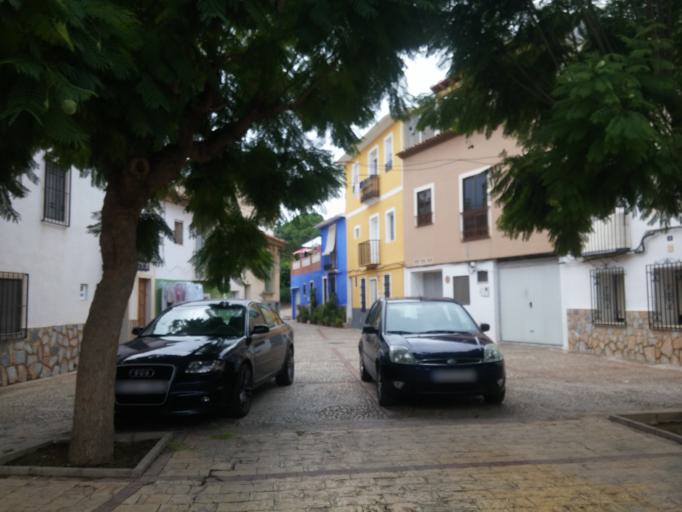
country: ES
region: Valencia
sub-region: Provincia de Alicante
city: Villajoyosa
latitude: 38.5032
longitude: -0.2357
